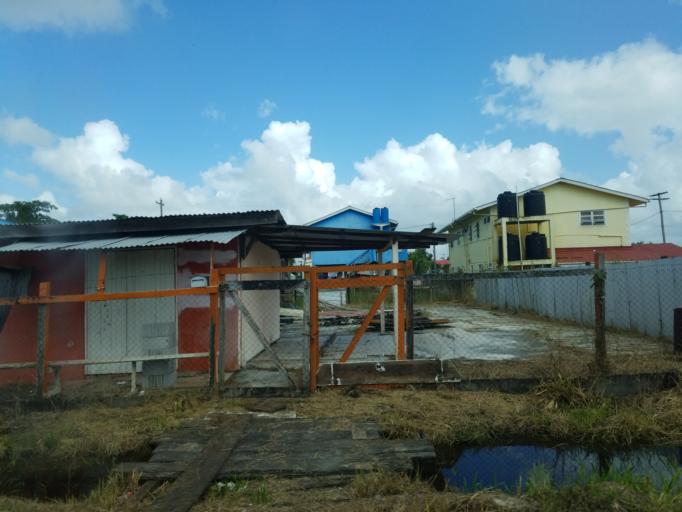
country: GY
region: Essequibo Islands-West Demerara
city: Vreed-en-Hoop
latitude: 6.7784
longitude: -58.2262
